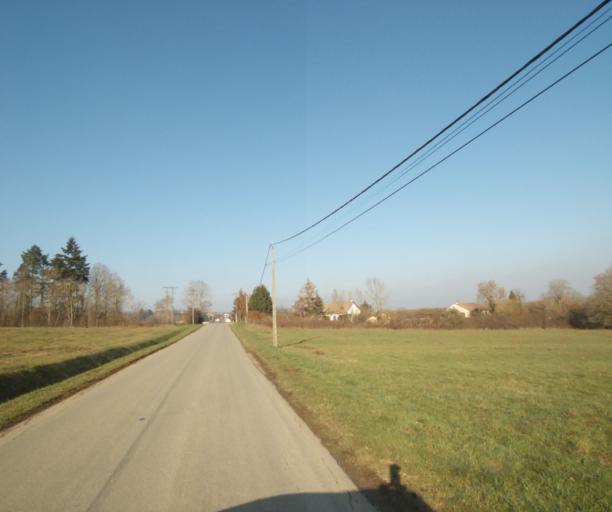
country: FR
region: Champagne-Ardenne
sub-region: Departement de la Haute-Marne
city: Wassy
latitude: 48.5086
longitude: 4.9216
